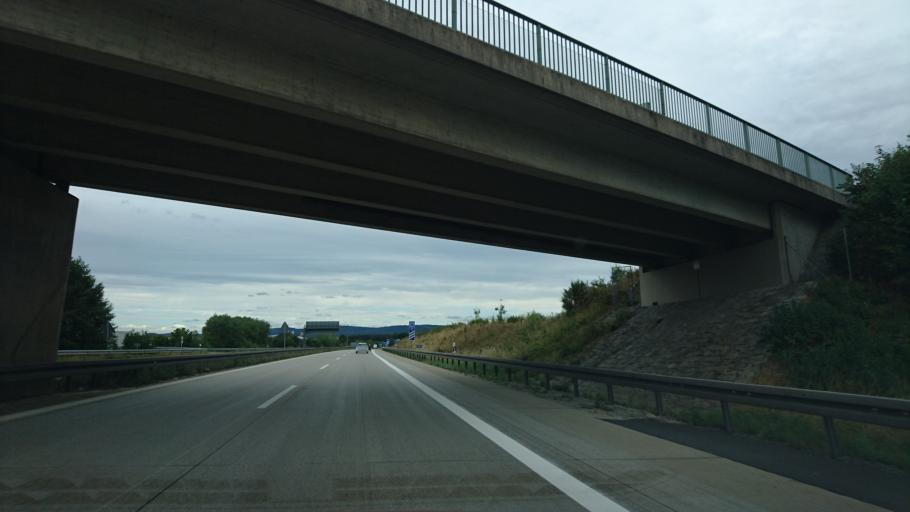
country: DE
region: Bavaria
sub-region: Upper Palatinate
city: Wernberg-Koblitz
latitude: 49.5280
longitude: 12.1483
